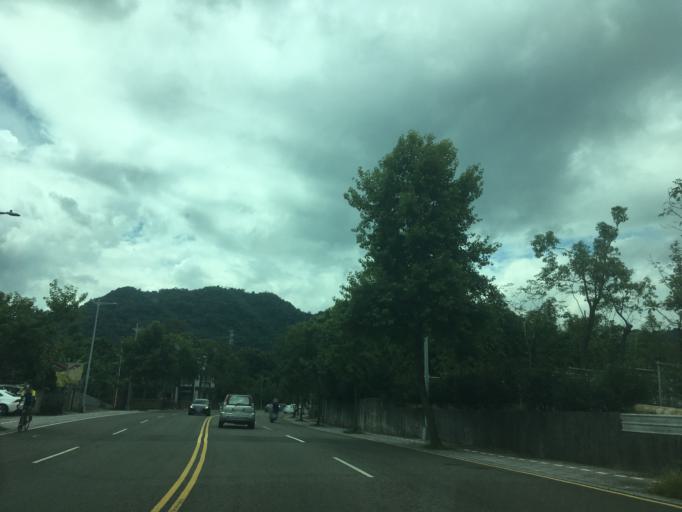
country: TW
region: Taiwan
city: Daxi
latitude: 24.8455
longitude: 121.2854
